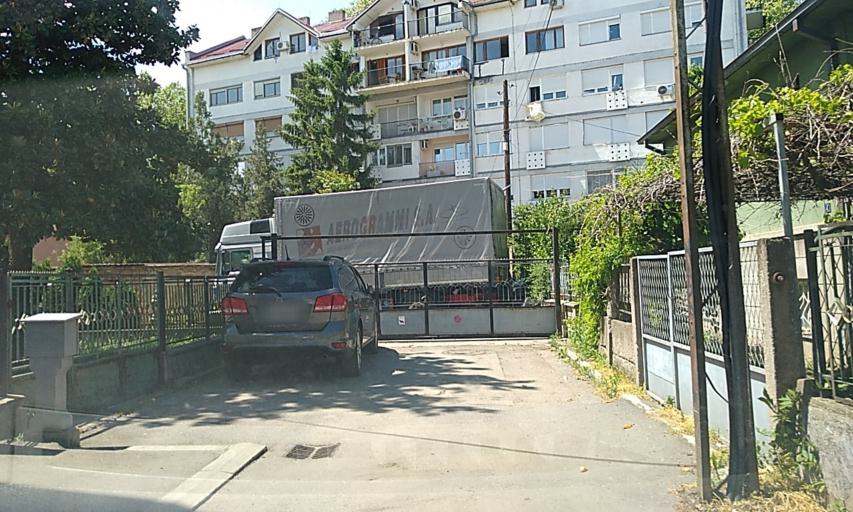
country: RS
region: Central Serbia
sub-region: Nisavski Okrug
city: Nis
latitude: 43.3139
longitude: 21.9022
